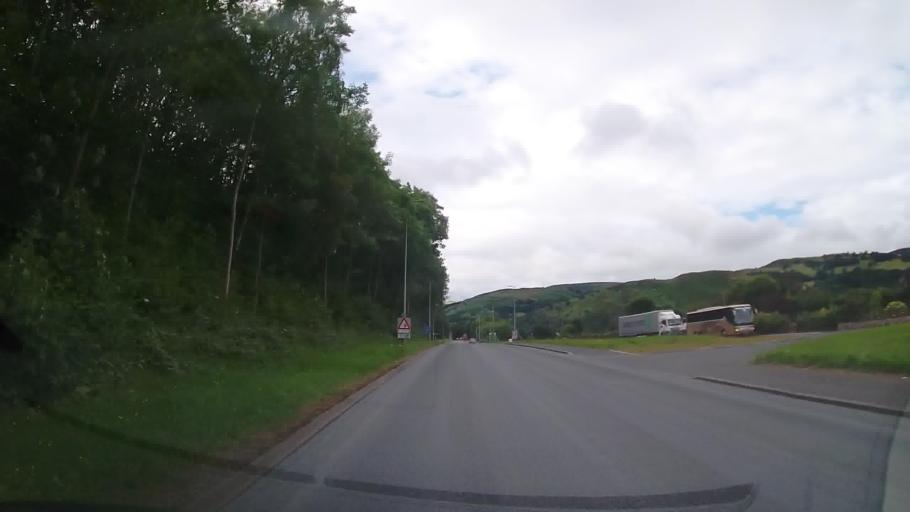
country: GB
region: Wales
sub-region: Denbighshire
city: Bryneglwys
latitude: 52.9721
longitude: -3.2541
